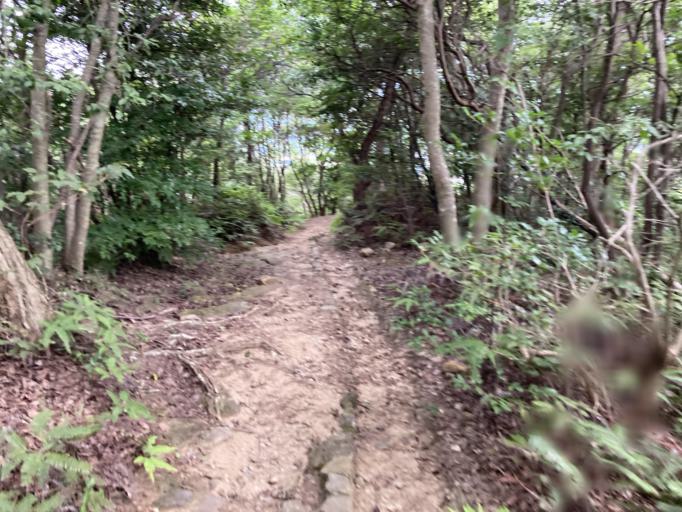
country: JP
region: Aichi
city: Nishio
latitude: 34.8481
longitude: 137.1210
